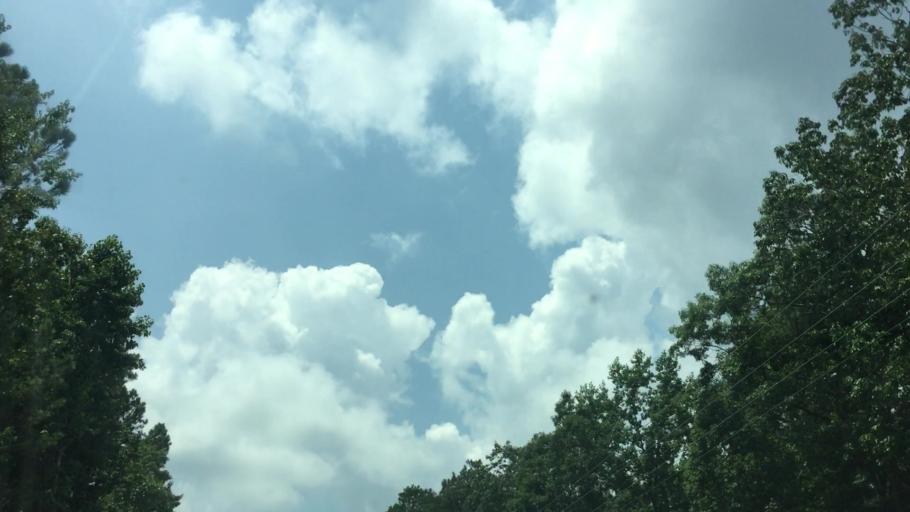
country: US
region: Georgia
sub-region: Carroll County
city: Villa Rica
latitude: 33.6151
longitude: -84.8826
